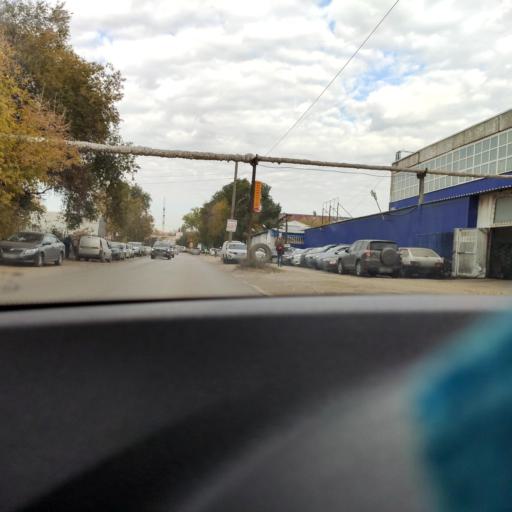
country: RU
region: Samara
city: Samara
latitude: 53.1973
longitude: 50.2586
